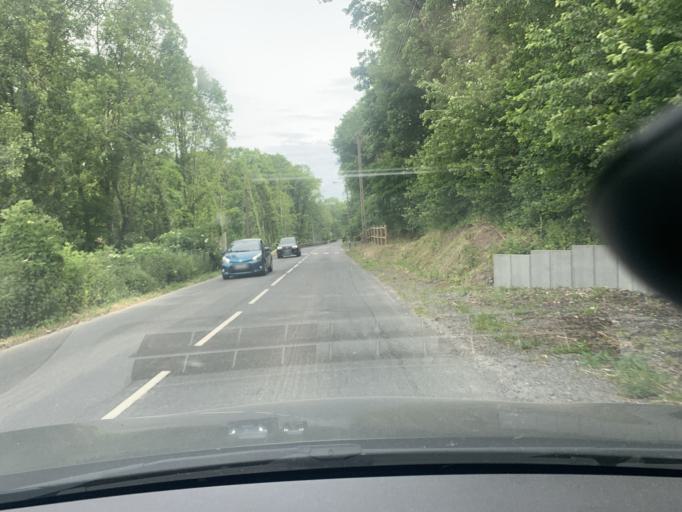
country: FR
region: Nord-Pas-de-Calais
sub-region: Departement du Nord
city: Marcoing
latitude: 50.1237
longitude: 3.1849
